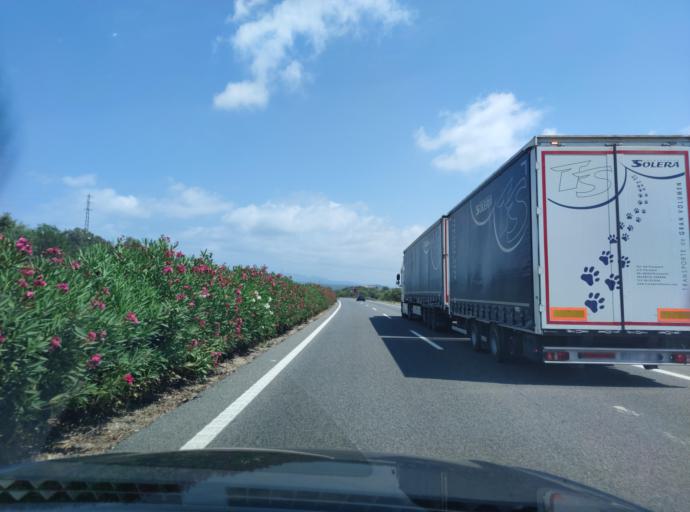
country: ES
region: Catalonia
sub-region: Provincia de Tarragona
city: Masdenverge
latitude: 40.7078
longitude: 0.5519
